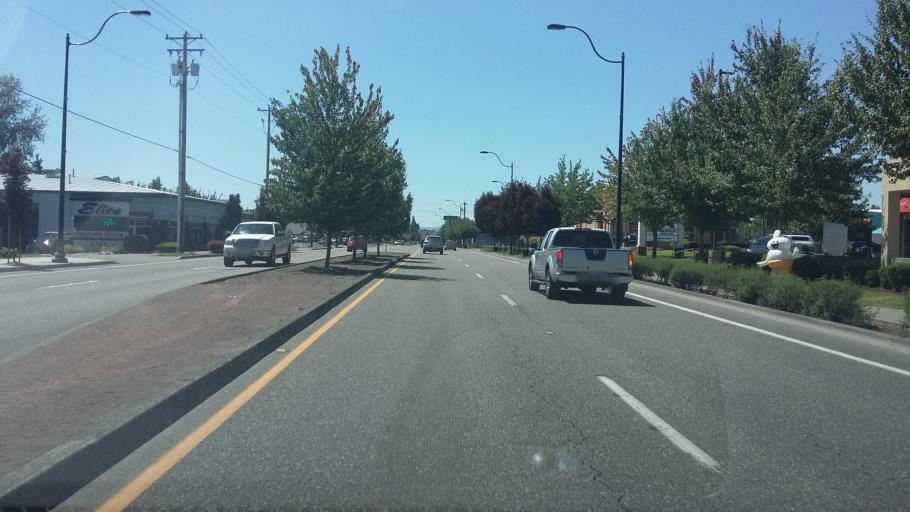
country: US
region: Washington
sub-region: Clark County
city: Battle Ground
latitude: 45.7807
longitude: -122.5539
